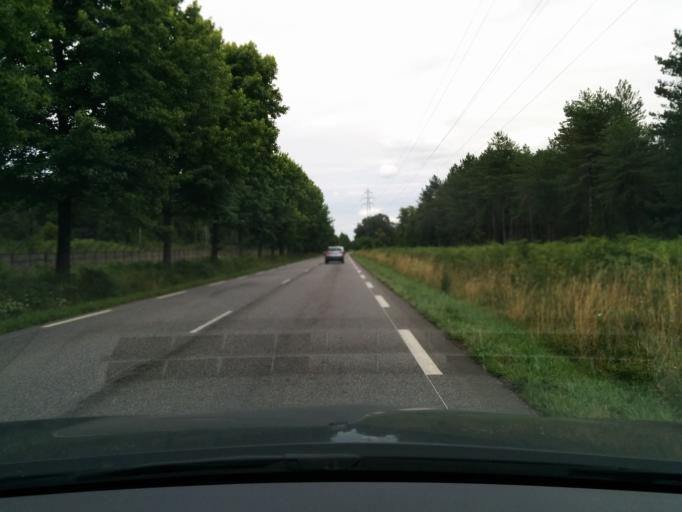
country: FR
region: Midi-Pyrenees
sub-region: Departement des Hautes-Pyrenees
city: La Barthe-de-Neste
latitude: 43.0851
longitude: 0.3680
